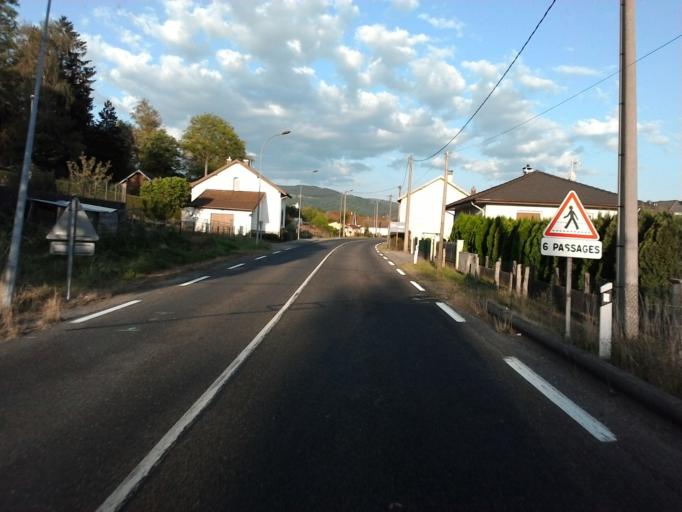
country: FR
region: Lorraine
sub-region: Departement des Vosges
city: Ramonchamp
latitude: 47.8956
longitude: 6.7329
